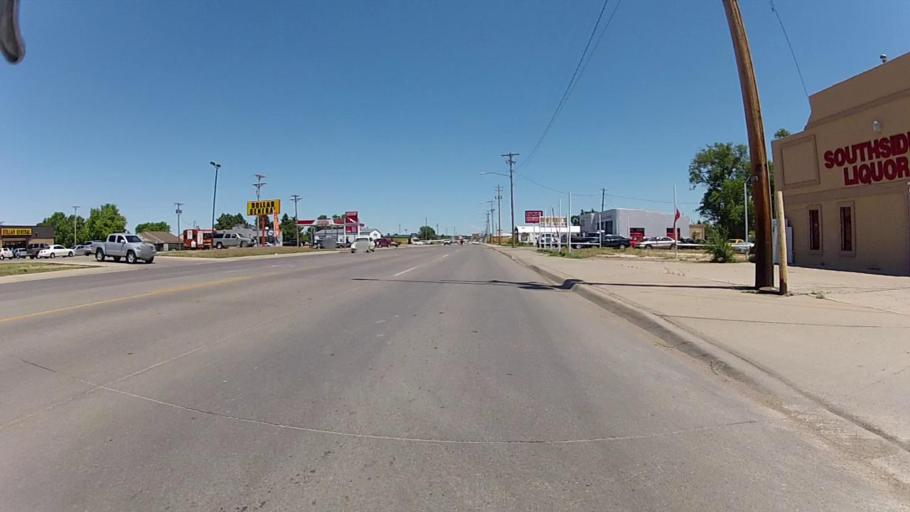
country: US
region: Kansas
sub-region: Ford County
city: Dodge City
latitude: 37.7388
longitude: -100.0194
